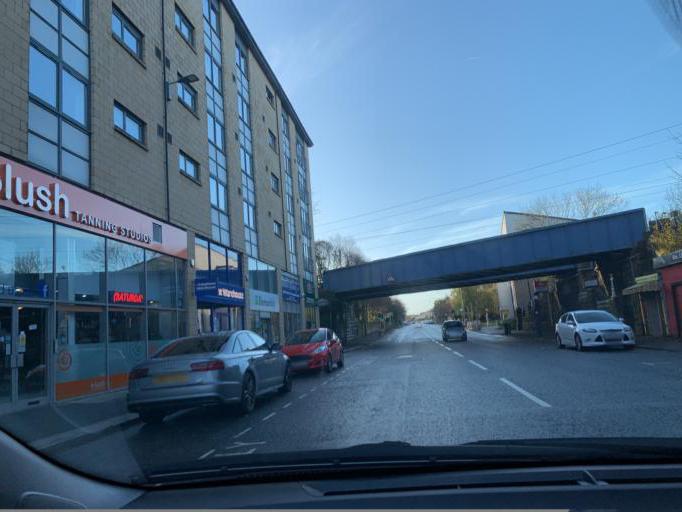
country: GB
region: Scotland
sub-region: East Renfrewshire
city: Giffnock
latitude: 55.8249
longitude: -4.2860
